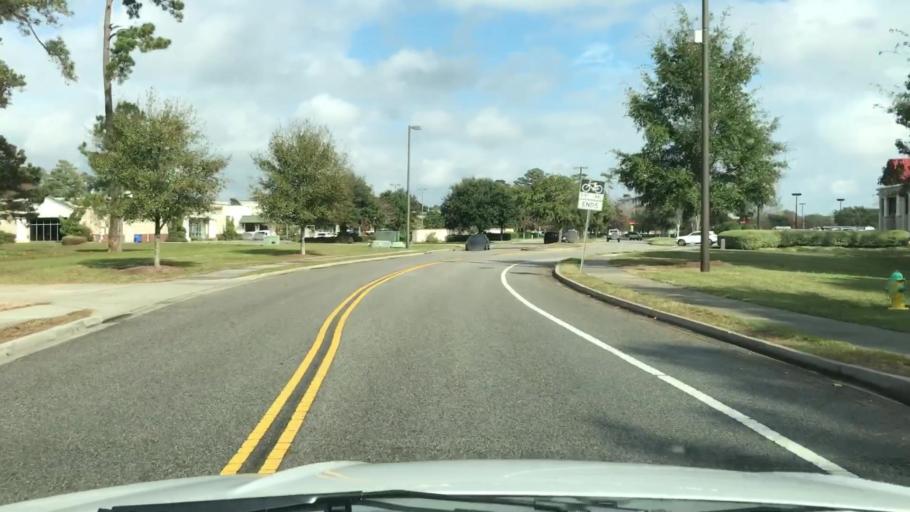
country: US
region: South Carolina
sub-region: Horry County
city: Myrtle Beach
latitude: 33.7251
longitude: -78.8722
